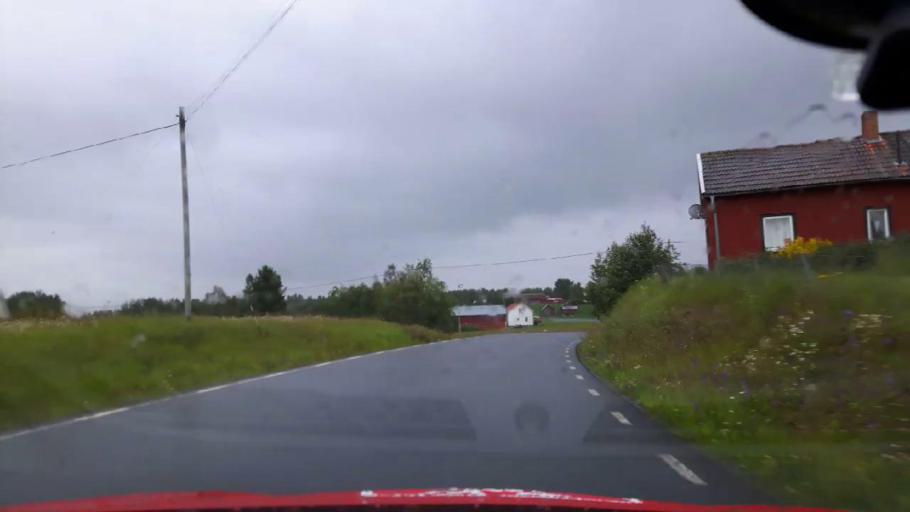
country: SE
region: Jaemtland
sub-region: OEstersunds Kommun
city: Brunflo
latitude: 63.0118
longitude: 14.7326
